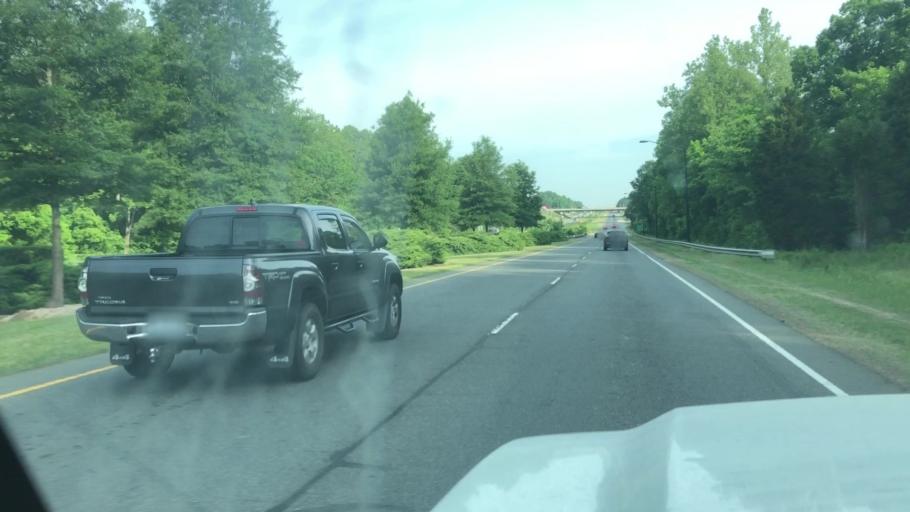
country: US
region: North Carolina
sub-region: Gaston County
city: Mount Holly
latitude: 35.3172
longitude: -80.9345
